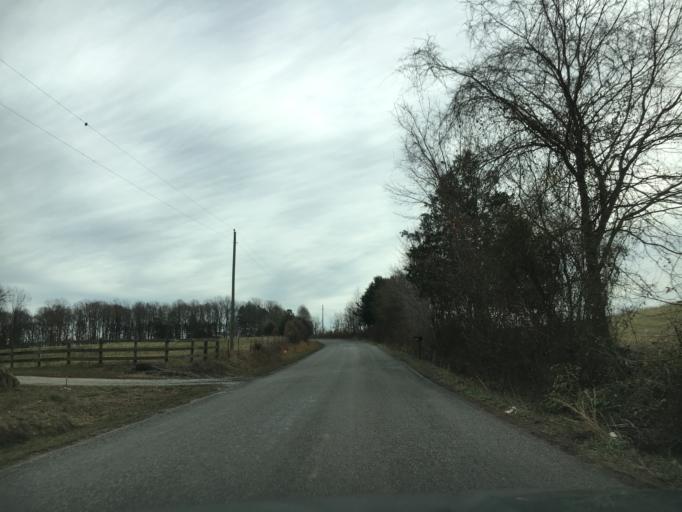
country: US
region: Virginia
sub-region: Amelia County
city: Amelia Court House
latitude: 37.4149
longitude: -77.9830
